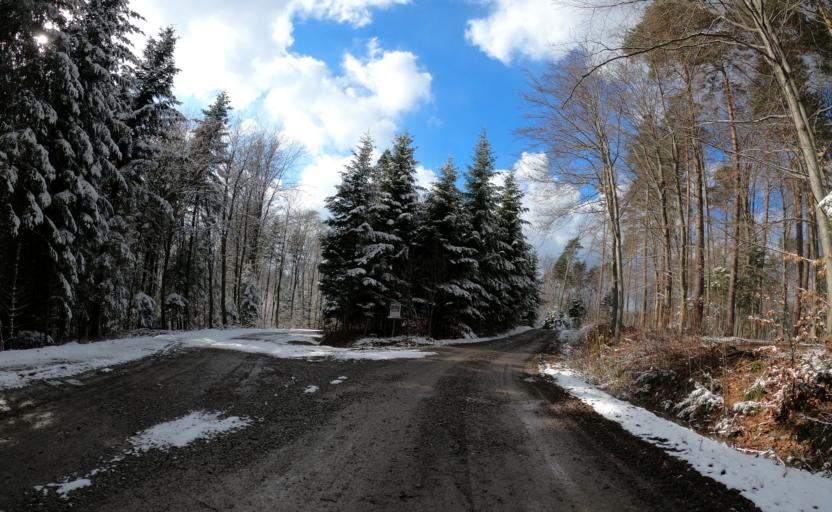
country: PL
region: Subcarpathian Voivodeship
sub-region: Powiat debicki
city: Debica
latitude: 49.9852
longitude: 21.3988
